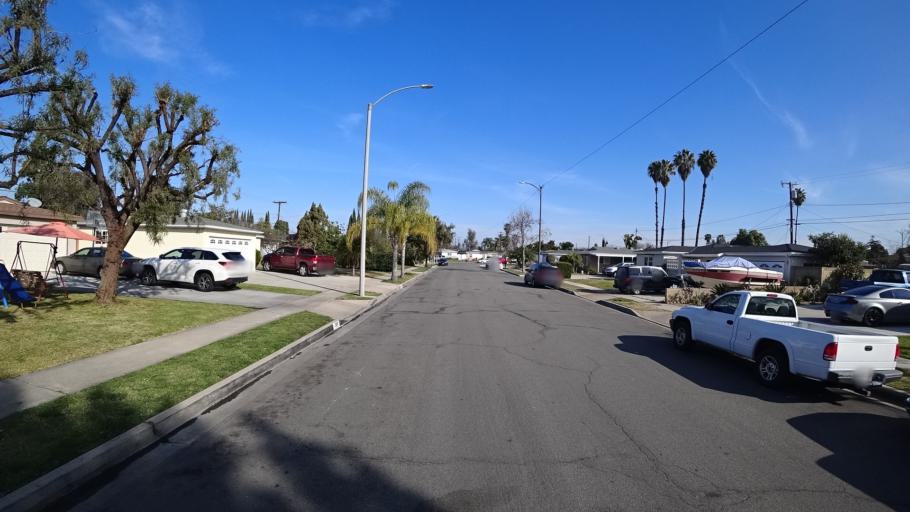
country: US
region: California
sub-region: Orange County
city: Fullerton
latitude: 33.8518
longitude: -117.9391
